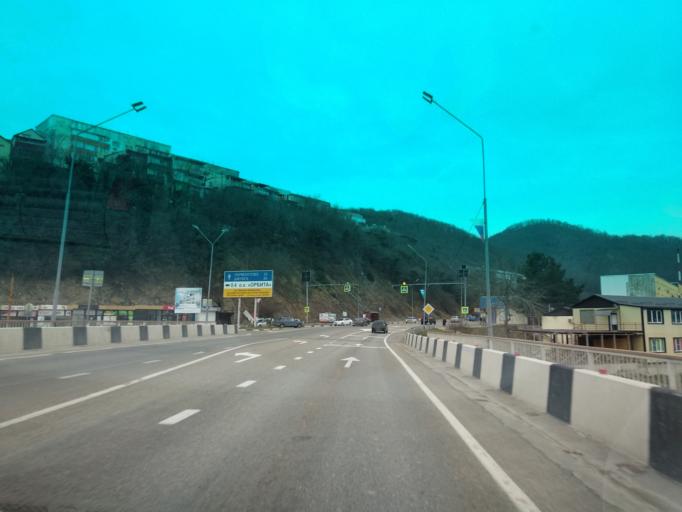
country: RU
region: Krasnodarskiy
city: Ol'ginka
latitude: 44.1991
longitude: 38.8886
